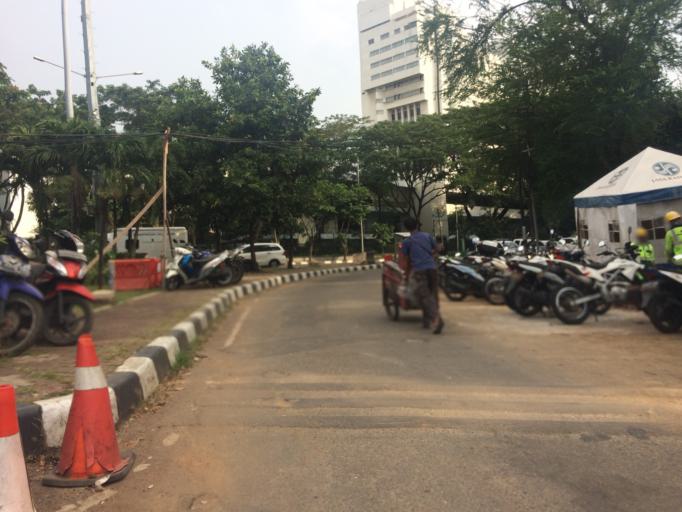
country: ID
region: Jakarta Raya
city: Jakarta
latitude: -6.1706
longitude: 106.8368
